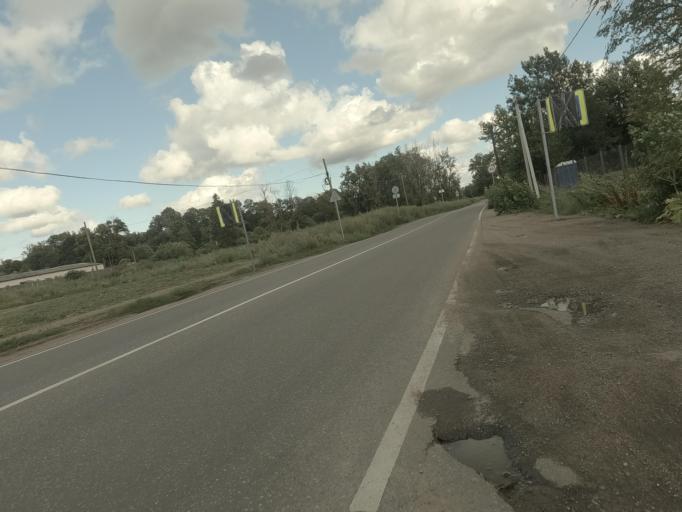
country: RU
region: Leningrad
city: Shcheglovo
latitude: 60.0291
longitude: 30.7562
